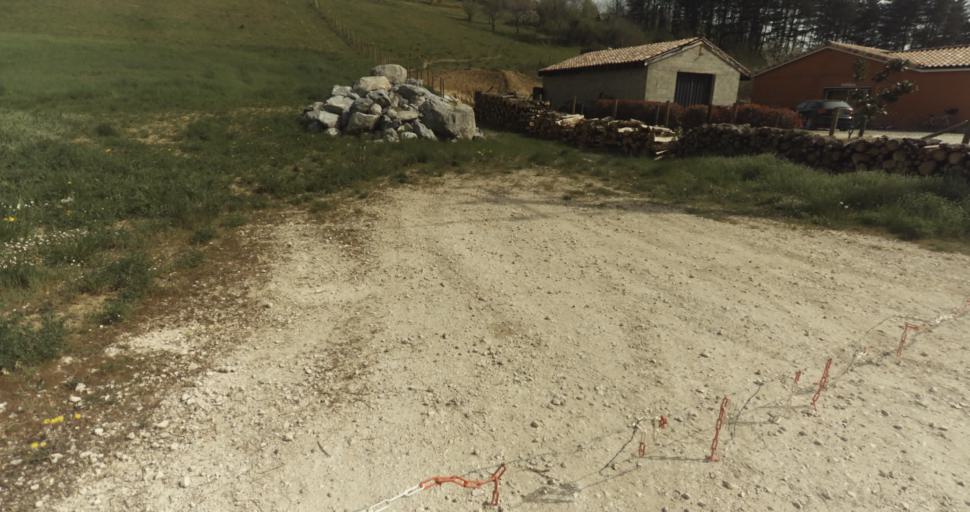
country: FR
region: Midi-Pyrenees
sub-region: Departement du Tarn-et-Garonne
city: Moissac
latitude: 44.1133
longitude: 1.0925
